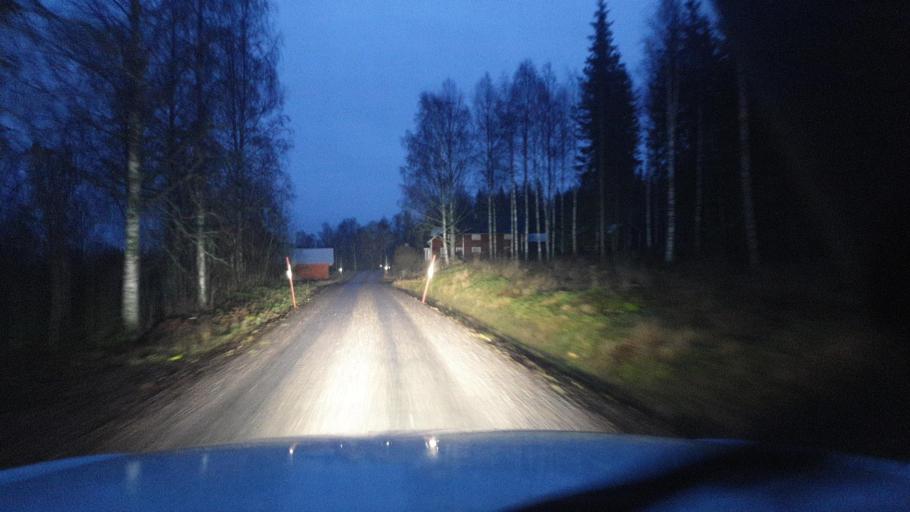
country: SE
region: Vaermland
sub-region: Torsby Kommun
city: Torsby
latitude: 59.9762
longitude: 12.8520
